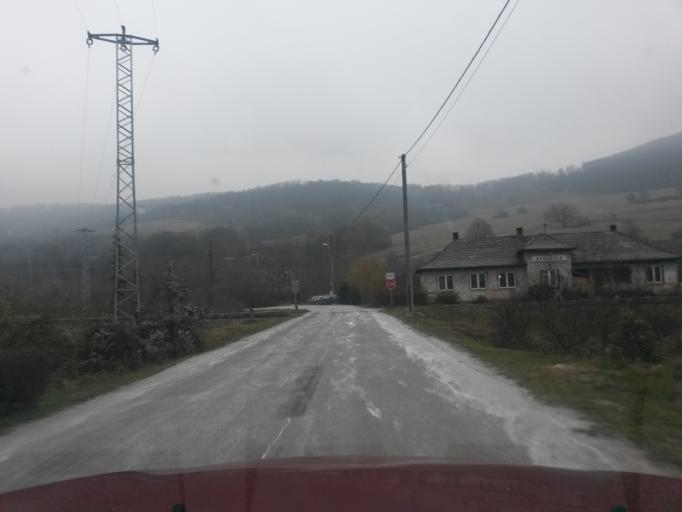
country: SK
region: Kosicky
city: Roznava
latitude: 48.6807
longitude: 20.5199
